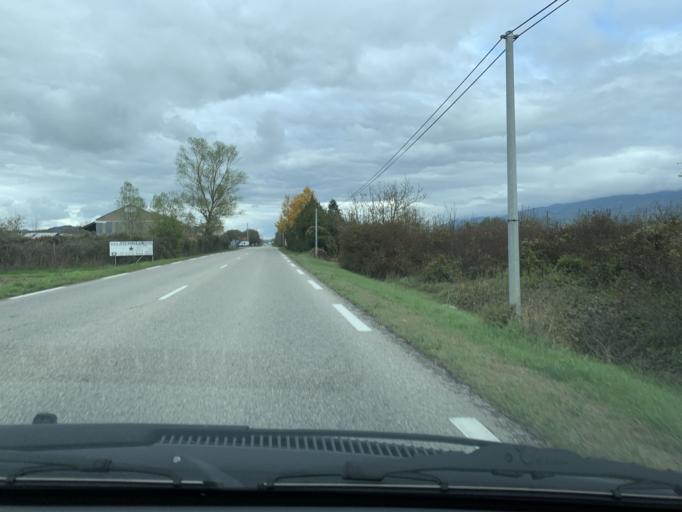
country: FR
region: Rhone-Alpes
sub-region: Departement de l'Isere
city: Saint-Hilaire-du-Rosier
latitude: 45.1175
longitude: 5.2708
